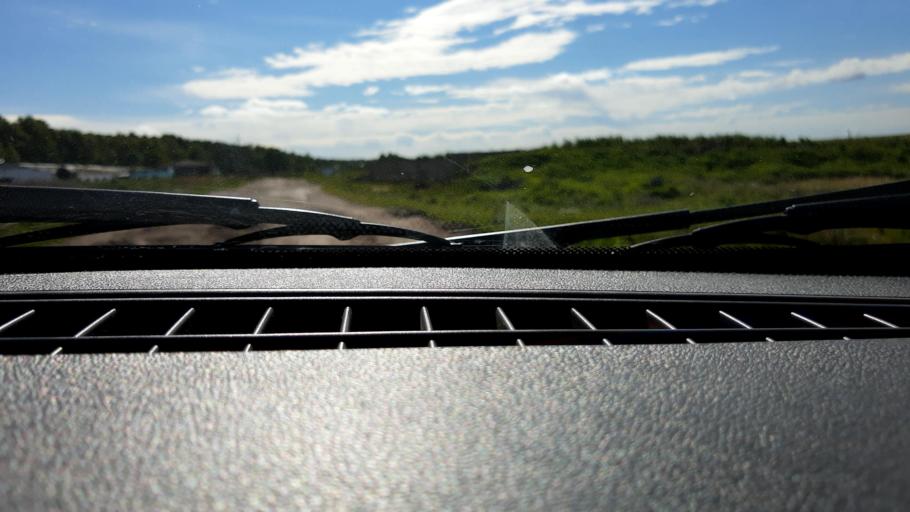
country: RU
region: Bashkortostan
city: Asanovo
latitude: 54.8211
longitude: 55.6234
